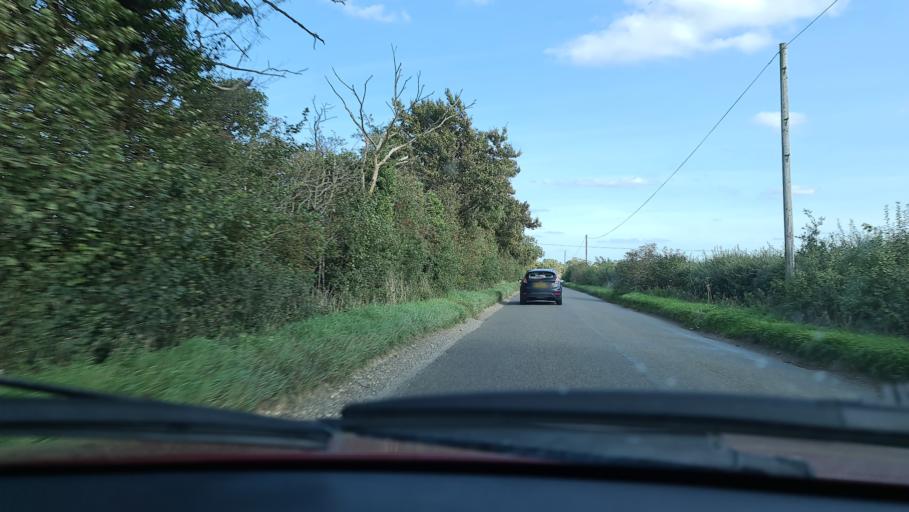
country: GB
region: England
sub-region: Northamptonshire
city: Brackley
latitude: 52.0134
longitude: -1.1637
